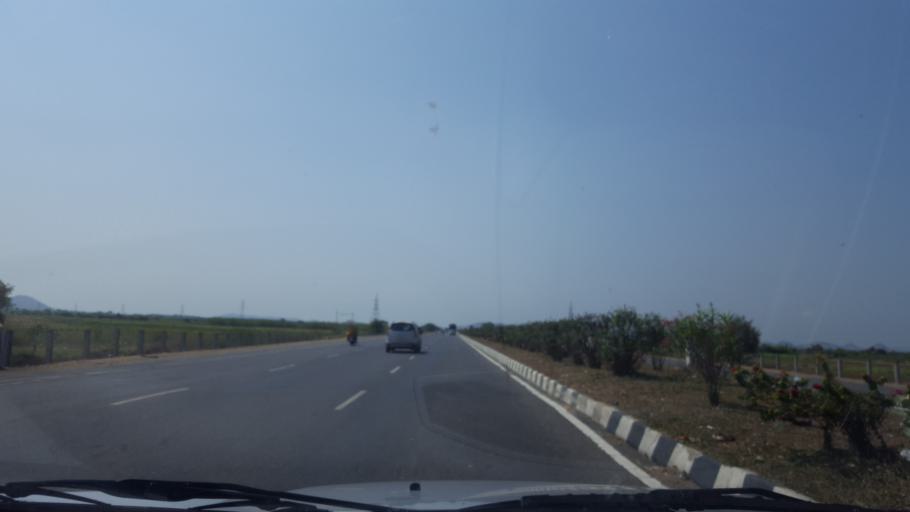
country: IN
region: Andhra Pradesh
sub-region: Guntur
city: Chilakalurupet
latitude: 16.0282
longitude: 80.1283
